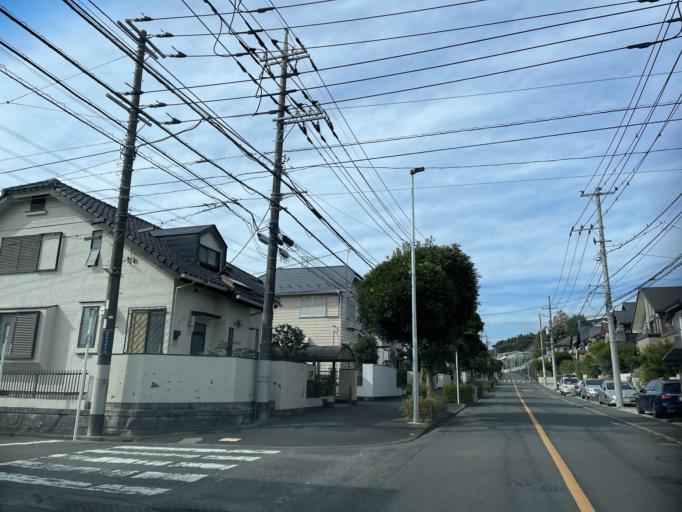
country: JP
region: Tokyo
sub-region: Machida-shi
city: Machida
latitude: 35.6101
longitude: 139.4784
